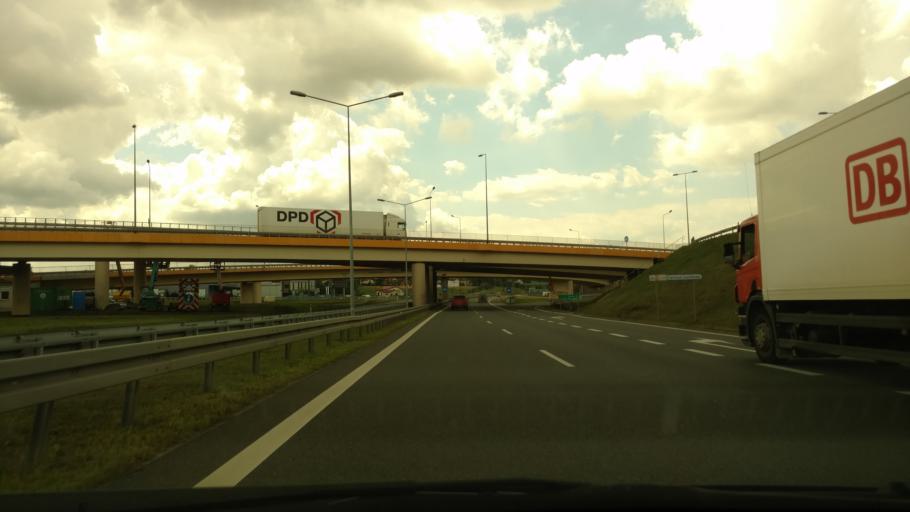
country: PL
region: Lesser Poland Voivodeship
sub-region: Powiat krakowski
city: Rzaska
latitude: 50.1083
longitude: 19.8413
